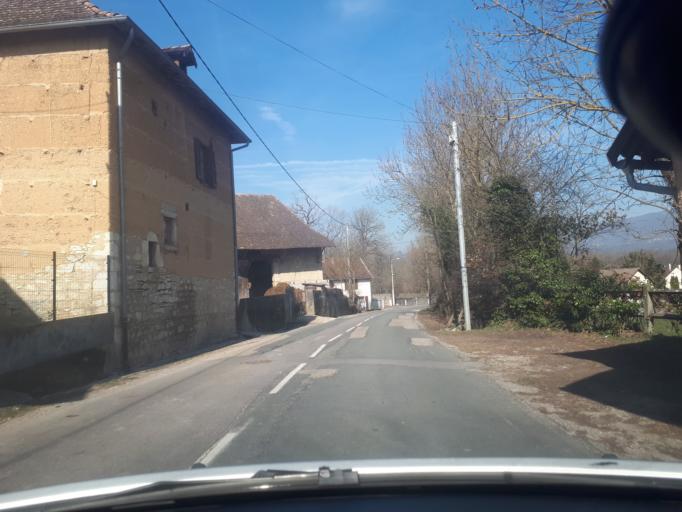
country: FR
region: Rhone-Alpes
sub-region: Departement de l'Isere
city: Thuellin
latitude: 45.6952
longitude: 5.5292
